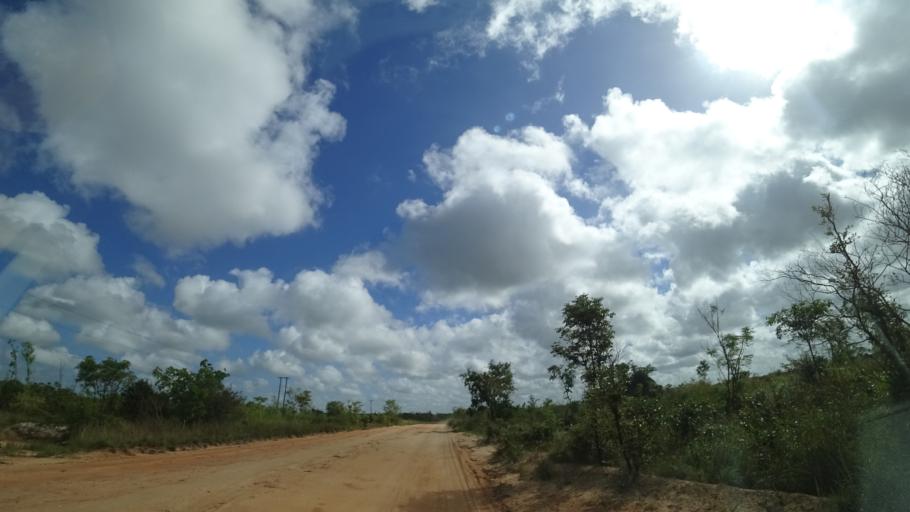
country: MZ
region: Sofala
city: Dondo
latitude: -19.4479
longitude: 34.7170
